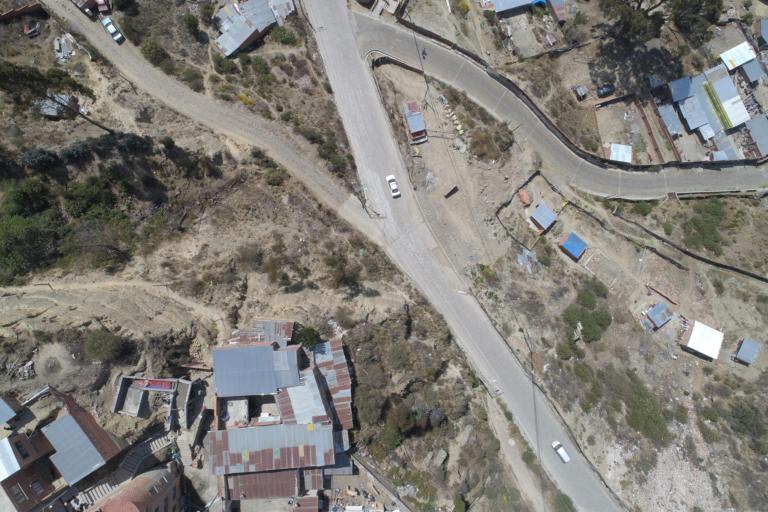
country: BO
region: La Paz
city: La Paz
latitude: -16.4989
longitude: -68.1001
